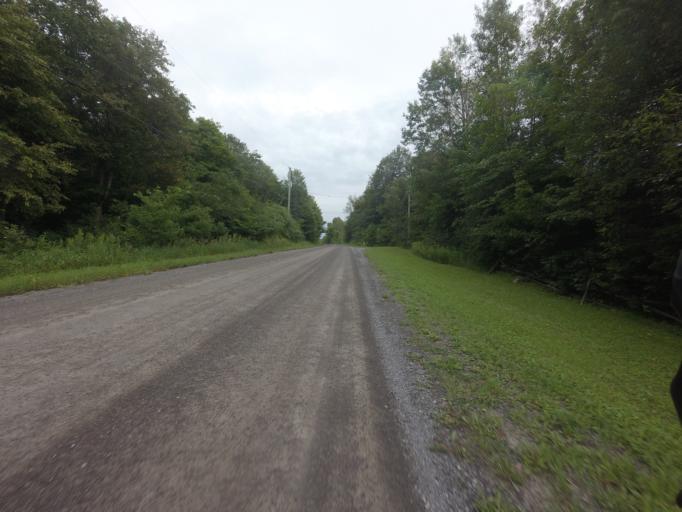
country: CA
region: Ontario
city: Carleton Place
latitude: 45.1664
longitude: -76.2760
